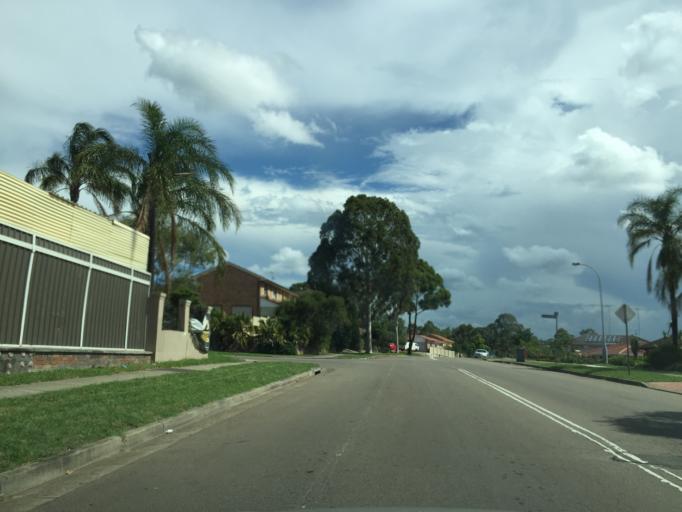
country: AU
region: New South Wales
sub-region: Blacktown
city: Doonside
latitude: -33.7736
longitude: 150.8770
